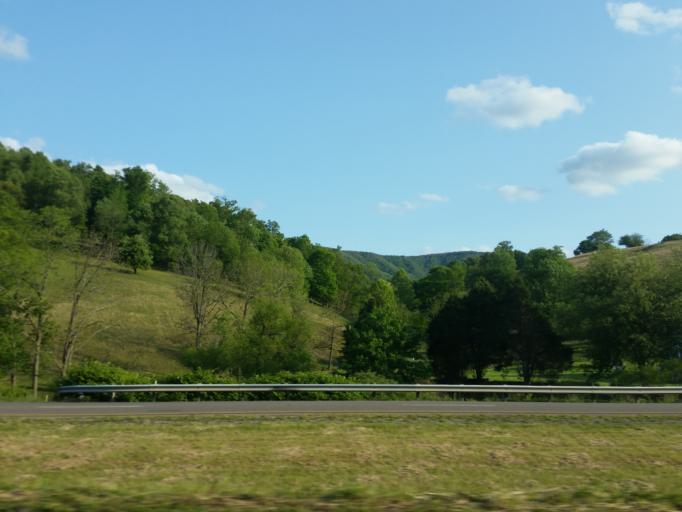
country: US
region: Virginia
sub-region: Tazewell County
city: Raven
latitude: 36.9807
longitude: -81.8620
